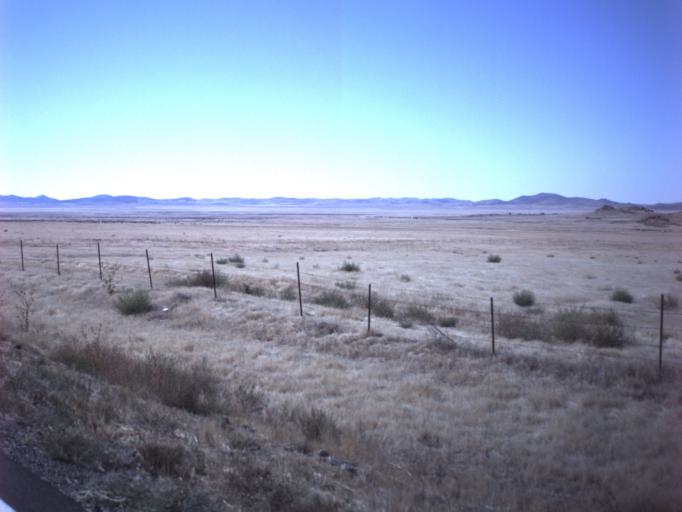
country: US
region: Utah
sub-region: Tooele County
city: Grantsville
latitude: 40.3901
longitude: -112.7474
